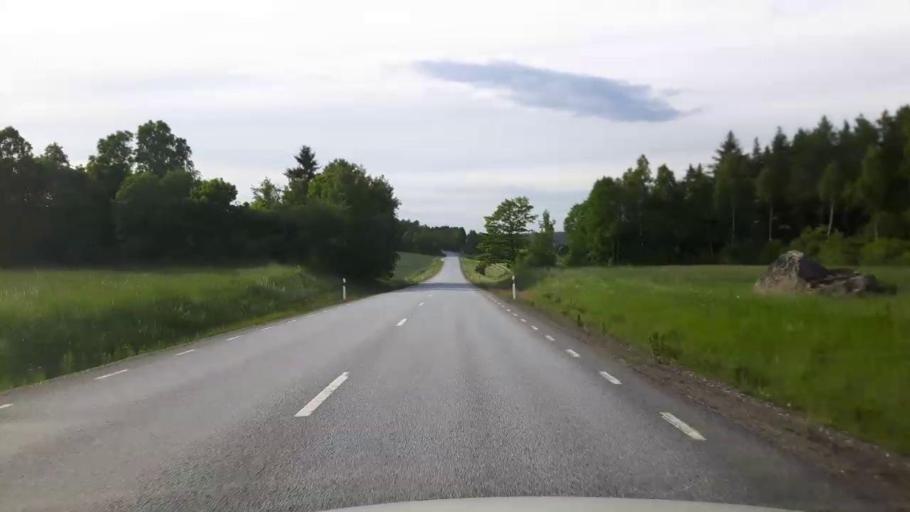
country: SE
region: Uppsala
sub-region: Habo Kommun
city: Balsta
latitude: 59.6456
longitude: 17.5666
